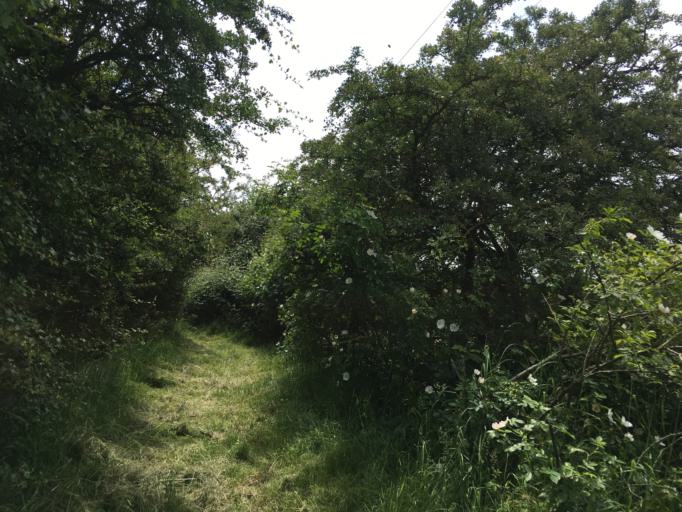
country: GB
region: England
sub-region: Kent
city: Queenborough
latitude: 51.3838
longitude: 0.7540
